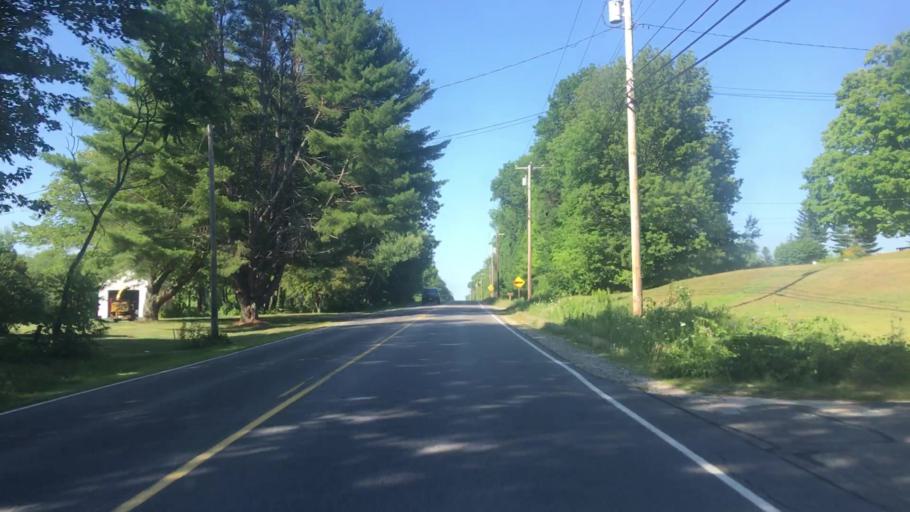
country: US
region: Maine
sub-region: York County
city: Buxton
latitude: 43.7432
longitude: -70.5432
